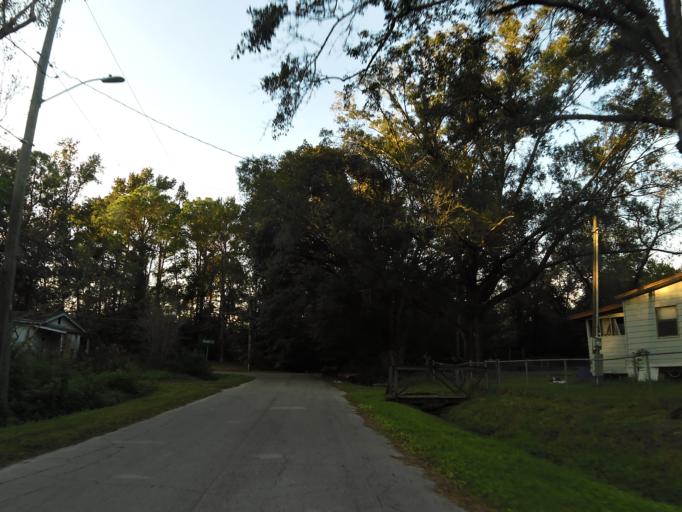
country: US
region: Florida
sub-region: Duval County
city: Jacksonville
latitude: 30.3618
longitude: -81.7348
